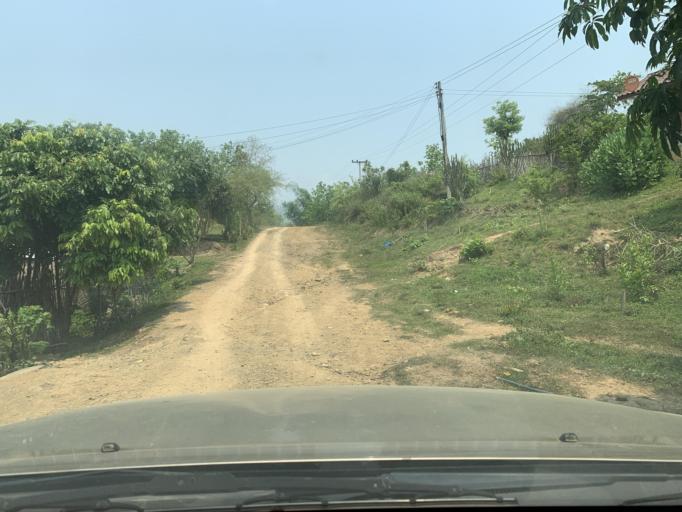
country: LA
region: Louangphabang
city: Louangphabang
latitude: 19.9466
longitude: 102.1339
